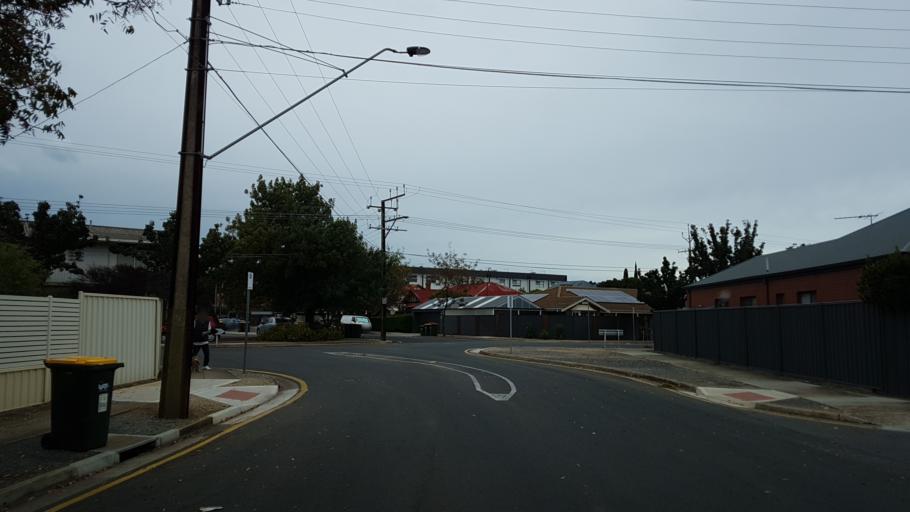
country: AU
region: South Australia
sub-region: Unley
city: Forestville
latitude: -34.9532
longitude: 138.5680
